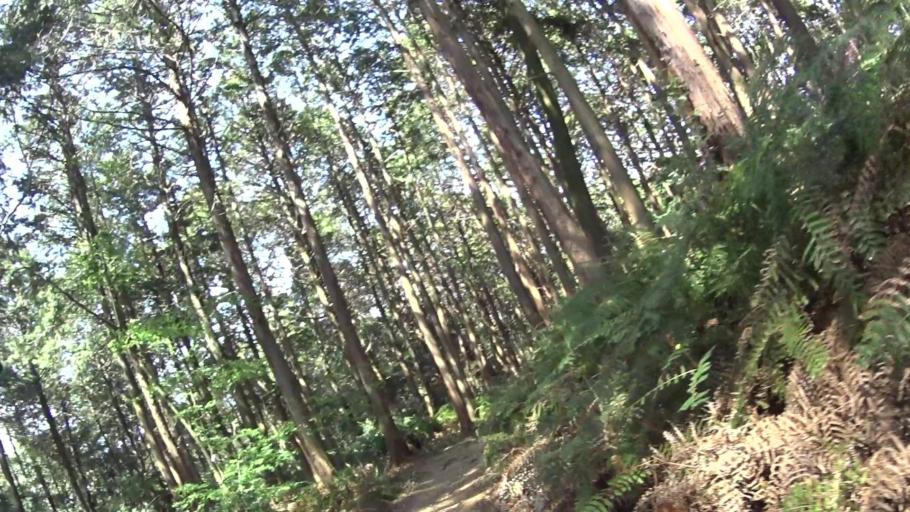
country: JP
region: Kyoto
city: Kyoto
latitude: 34.9938
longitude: 135.7879
